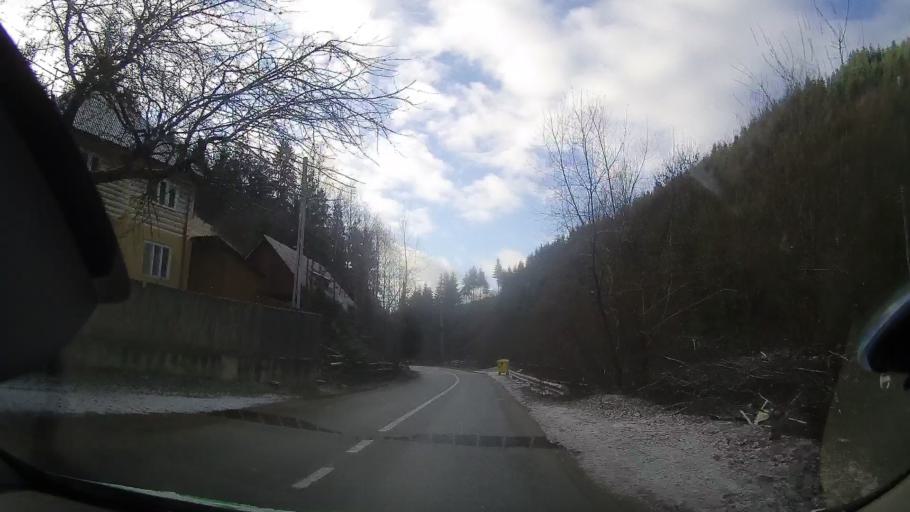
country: RO
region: Alba
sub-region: Comuna Albac
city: Albac
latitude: 46.4568
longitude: 22.9750
